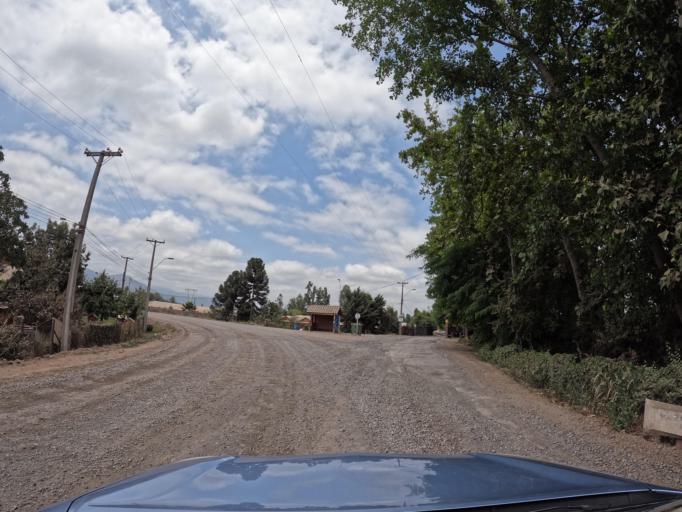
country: CL
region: O'Higgins
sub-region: Provincia de Colchagua
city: Chimbarongo
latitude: -34.7404
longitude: -70.9779
